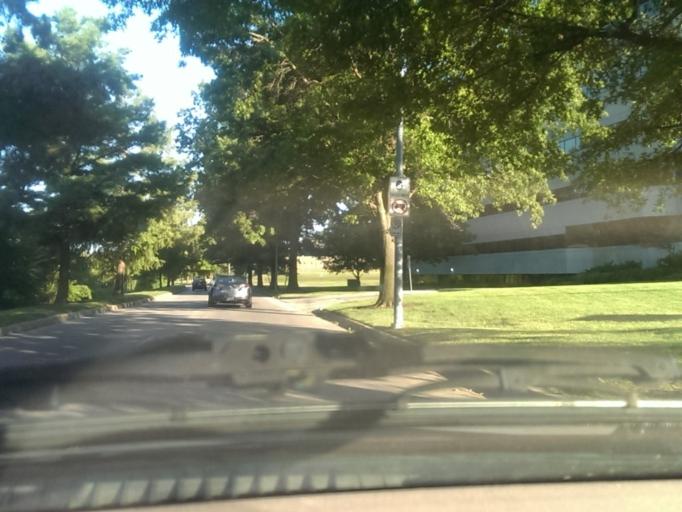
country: US
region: Kansas
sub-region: Johnson County
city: Leawood
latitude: 38.9627
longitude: -94.6038
